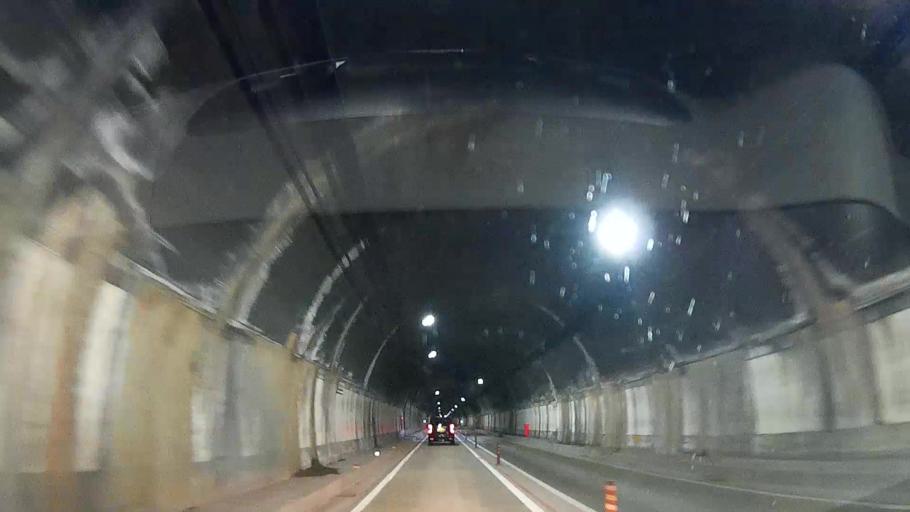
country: JP
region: Saitama
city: Chichibu
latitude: 35.9505
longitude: 139.1768
